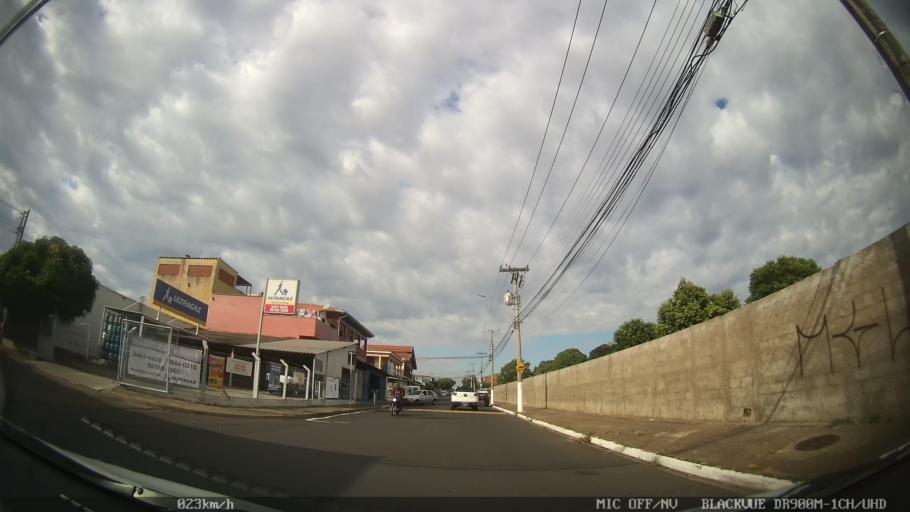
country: BR
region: Sao Paulo
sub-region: Americana
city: Americana
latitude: -22.7178
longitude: -47.3593
